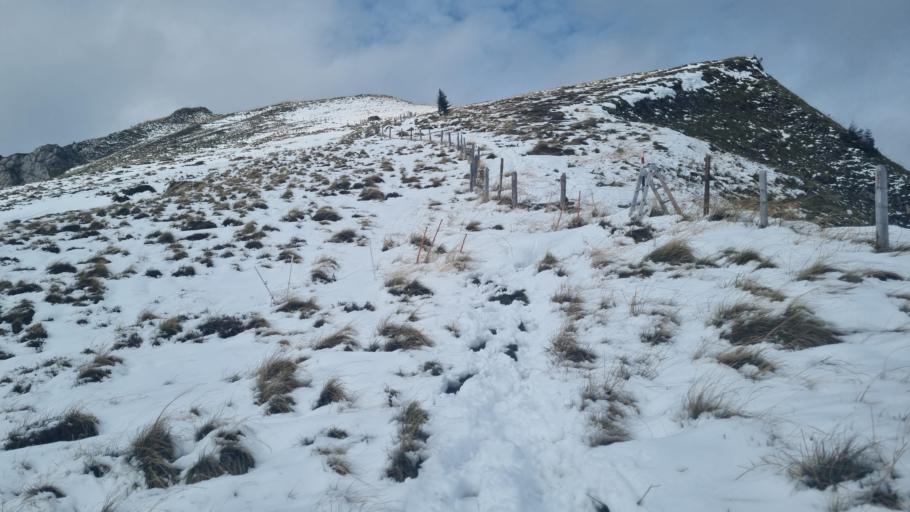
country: CH
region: Schwyz
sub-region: Bezirk March
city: Vorderthal
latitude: 47.0989
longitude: 8.9586
